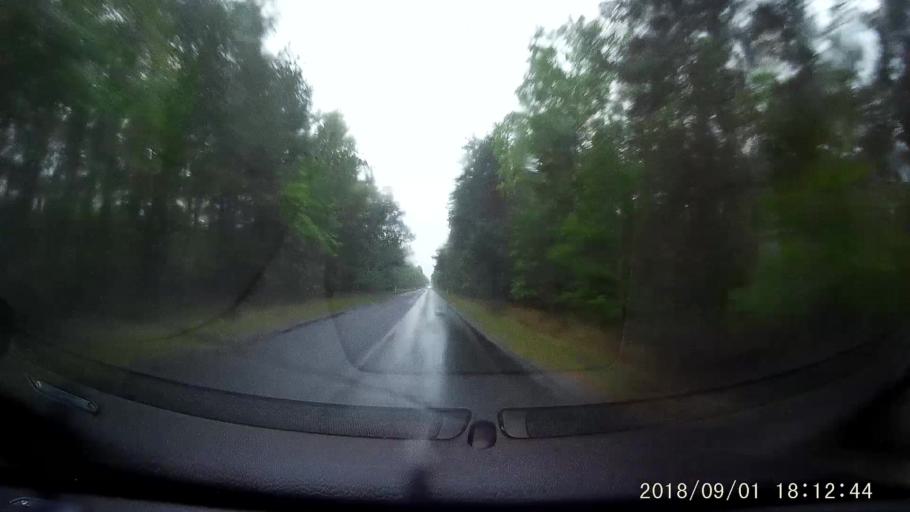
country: PL
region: Lower Silesian Voivodeship
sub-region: Powiat zgorzelecki
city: Piensk
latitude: 51.3098
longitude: 15.0680
